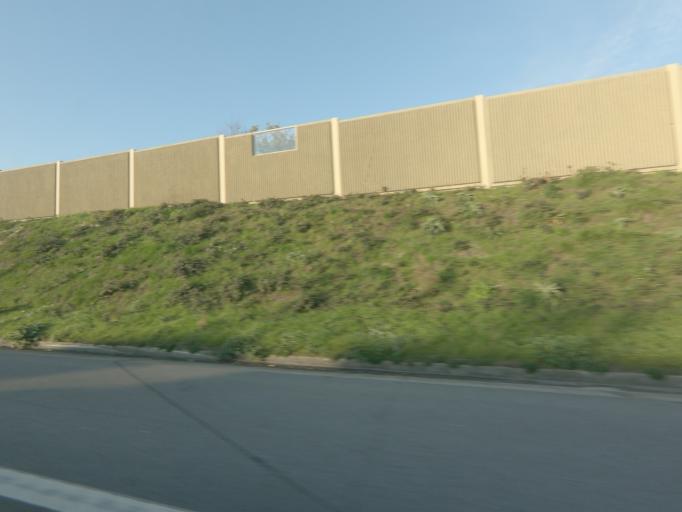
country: PT
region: Porto
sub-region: Lousada
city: Meinedo
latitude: 41.2197
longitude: -8.2451
